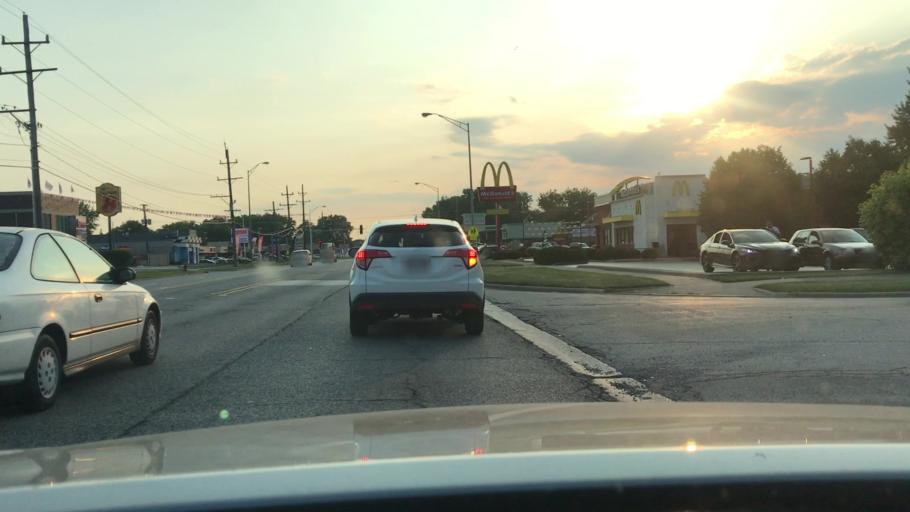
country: US
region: Illinois
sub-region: Cook County
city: Bridgeview
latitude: 41.7478
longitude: -87.8166
